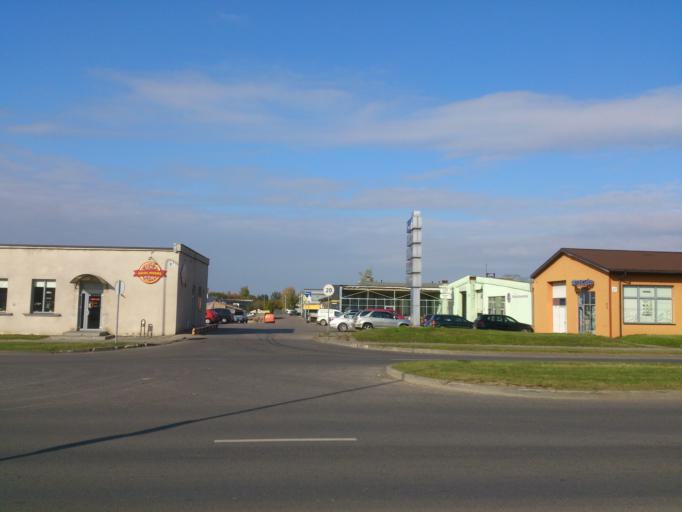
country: LT
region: Kauno apskritis
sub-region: Kaunas
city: Aleksotas
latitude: 54.8753
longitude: 23.9017
